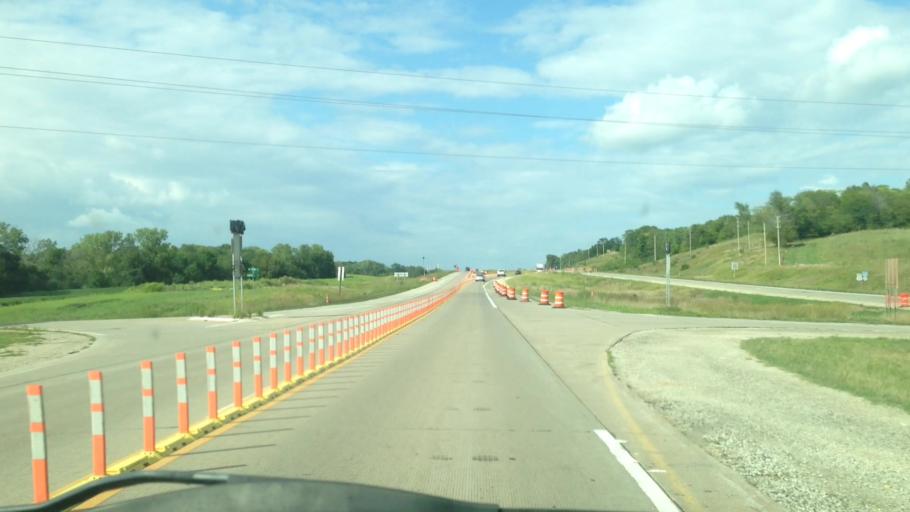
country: US
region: Iowa
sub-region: Henry County
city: Mount Pleasant
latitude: 40.9029
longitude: -91.5548
